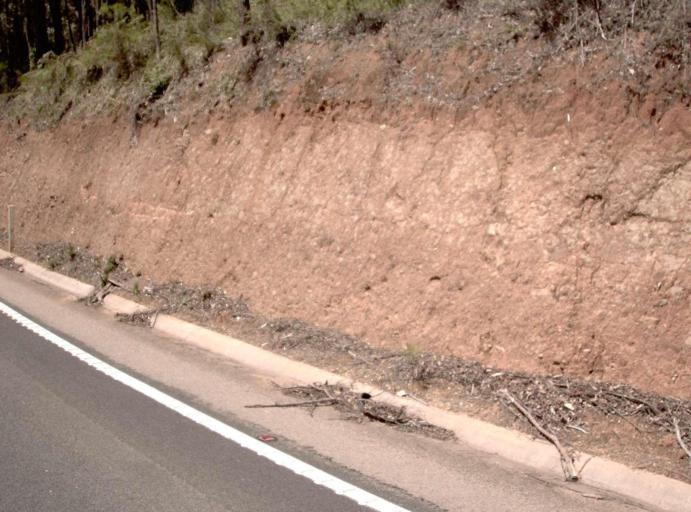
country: AU
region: New South Wales
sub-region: Bombala
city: Bombala
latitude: -37.5990
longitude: 148.9072
